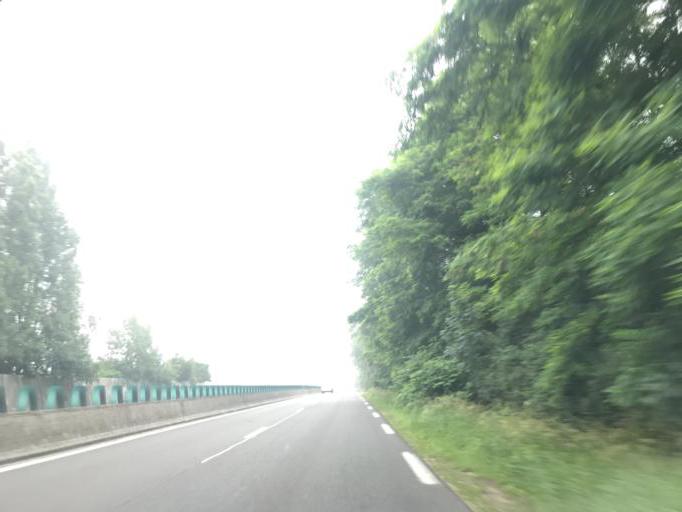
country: FR
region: Ile-de-France
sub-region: Departement de Seine-et-Marne
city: Lagny-sur-Marne
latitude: 48.8711
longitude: 2.7153
